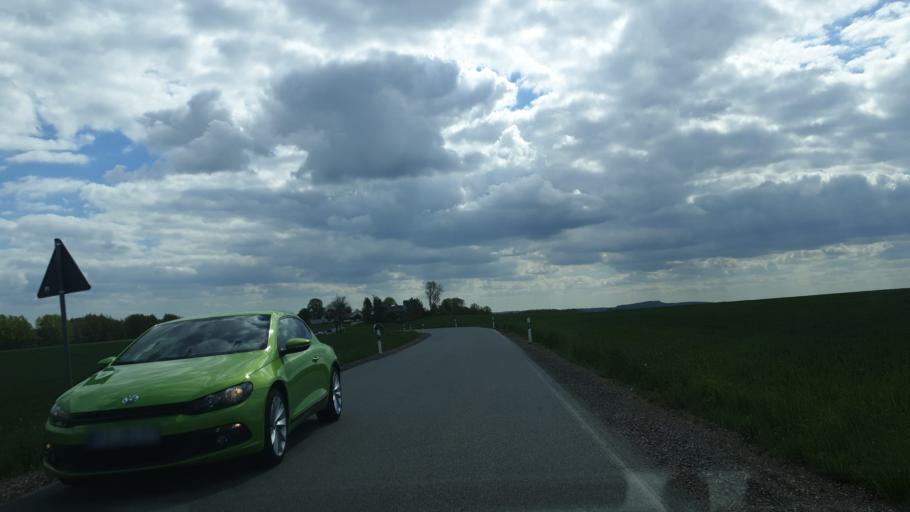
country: DE
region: Saxony
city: Lugau
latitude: 50.7555
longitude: 12.7666
